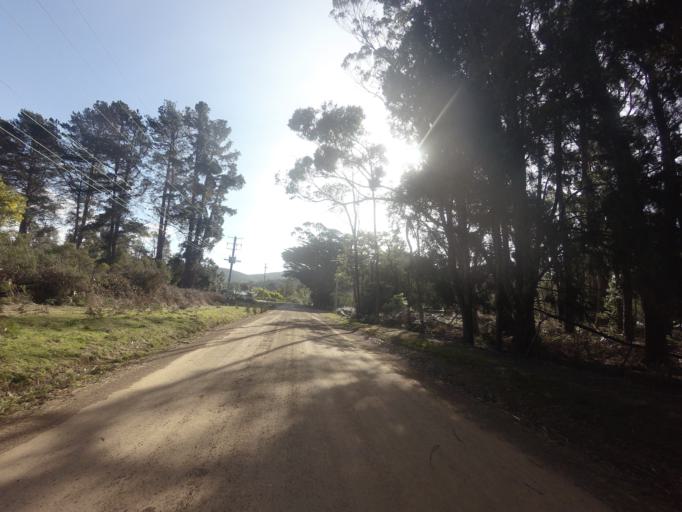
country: AU
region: Tasmania
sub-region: Kingborough
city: Kettering
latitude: -43.1106
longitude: 147.2575
